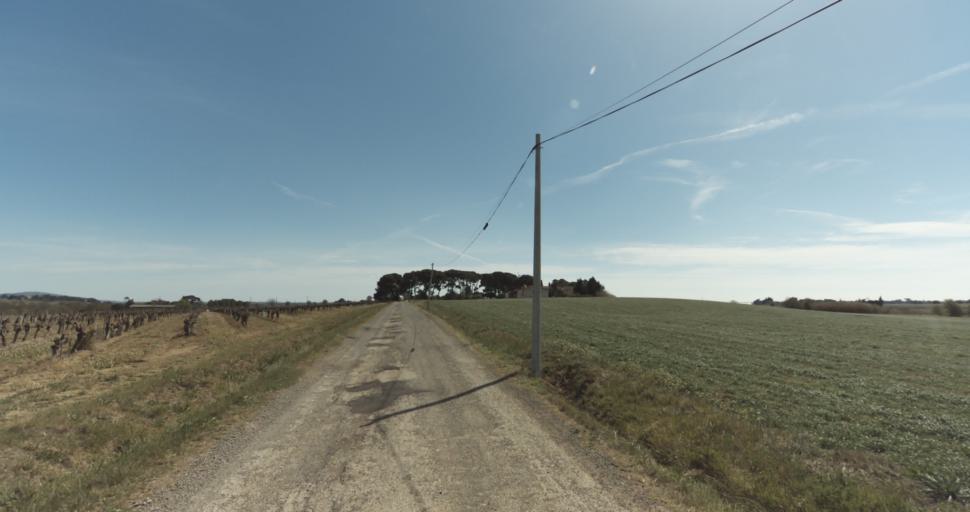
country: FR
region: Languedoc-Roussillon
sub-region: Departement de l'Herault
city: Pinet
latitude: 43.3981
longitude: 3.5405
